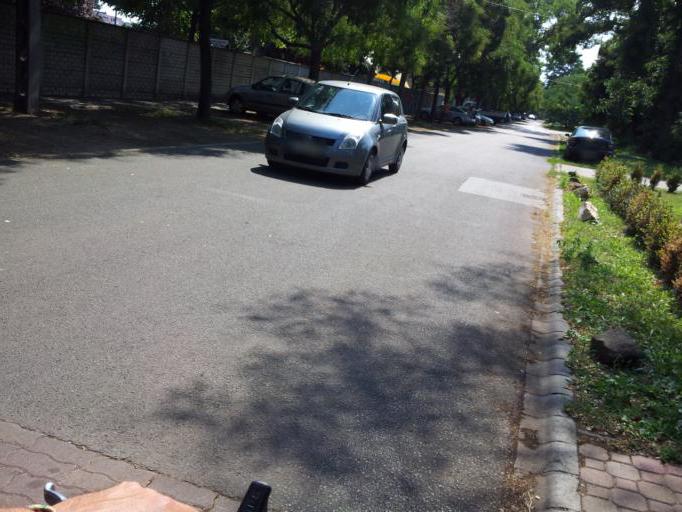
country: HU
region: Budapest
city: Budapest XIV. keruelet
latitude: 47.5122
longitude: 19.1174
